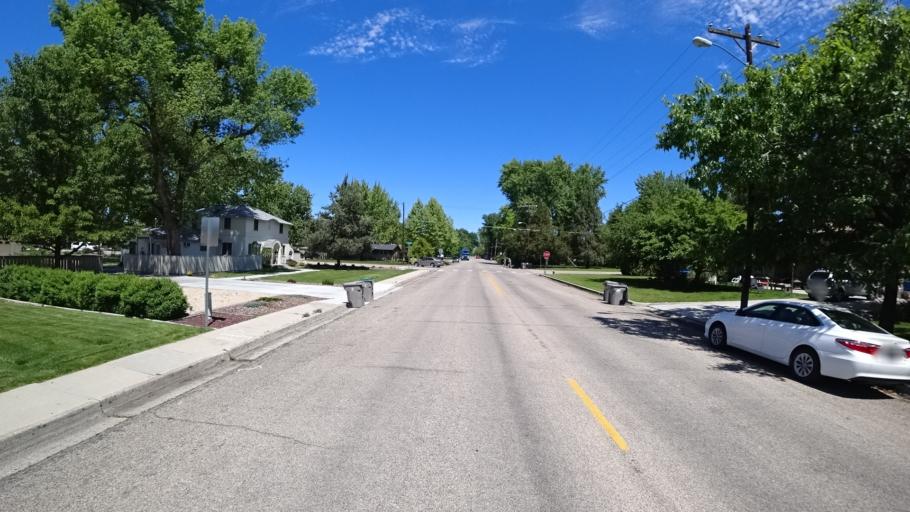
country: US
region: Idaho
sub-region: Ada County
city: Boise
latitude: 43.5966
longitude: -116.2236
